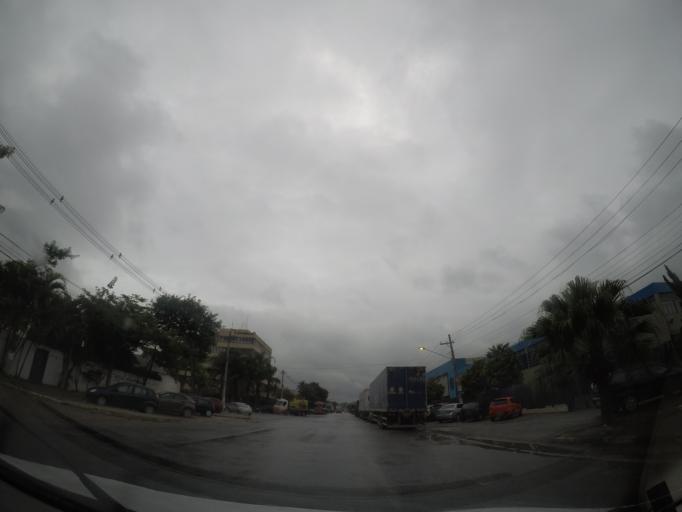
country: BR
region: Sao Paulo
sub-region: Guarulhos
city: Guarulhos
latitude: -23.4788
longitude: -46.4647
